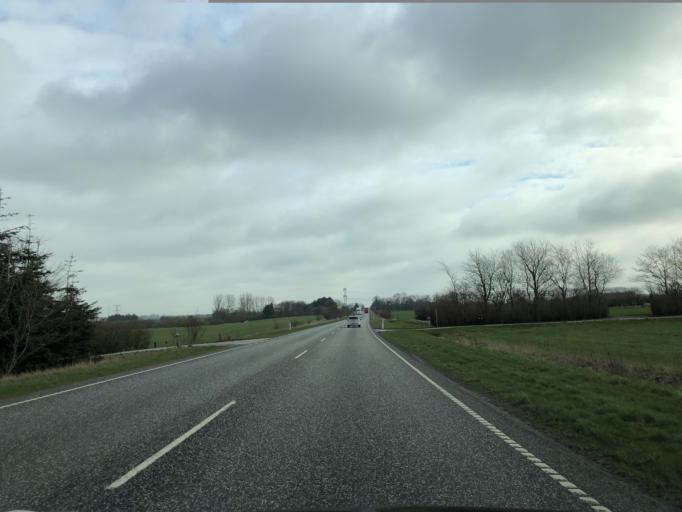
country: DK
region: North Denmark
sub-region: Vesthimmerland Kommune
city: Aars
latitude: 56.7900
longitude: 9.6052
